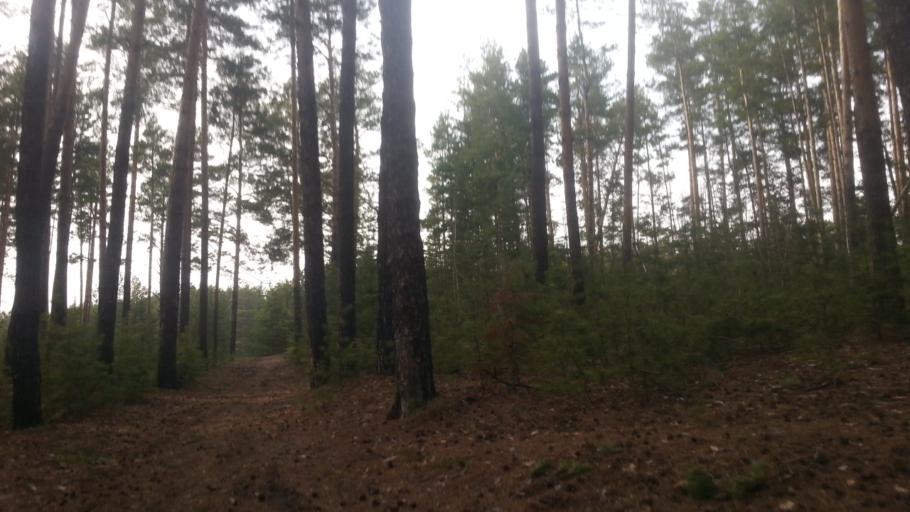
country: RU
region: Altai Krai
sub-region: Gorod Barnaulskiy
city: Barnaul
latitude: 53.3240
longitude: 83.7171
